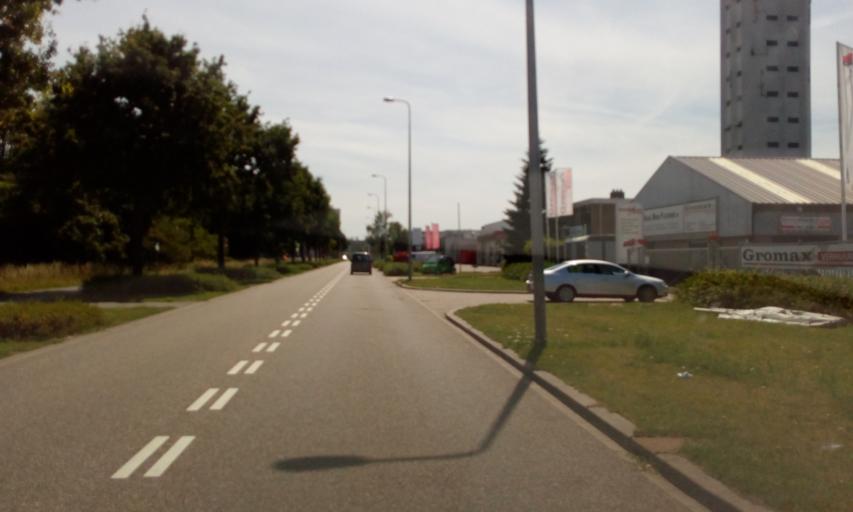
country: NL
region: South Holland
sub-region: Gemeente Alphen aan den Rijn
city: Alphen aan den Rijn
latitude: 52.1384
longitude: 4.6468
